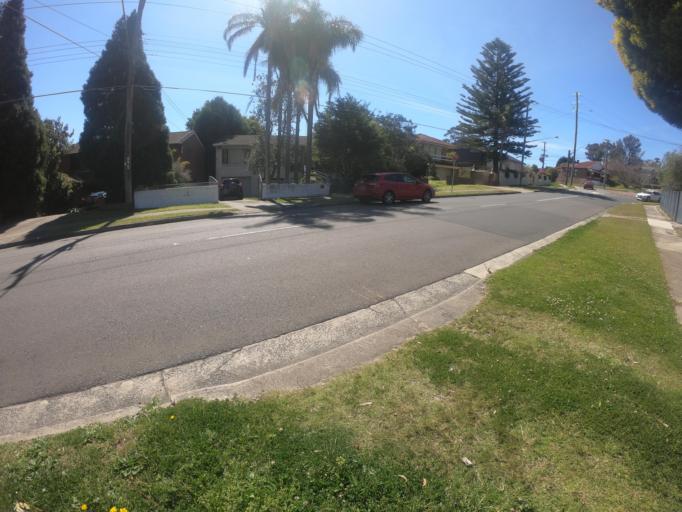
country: AU
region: New South Wales
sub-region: Ryde
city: East Ryde
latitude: -33.8190
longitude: 151.1276
